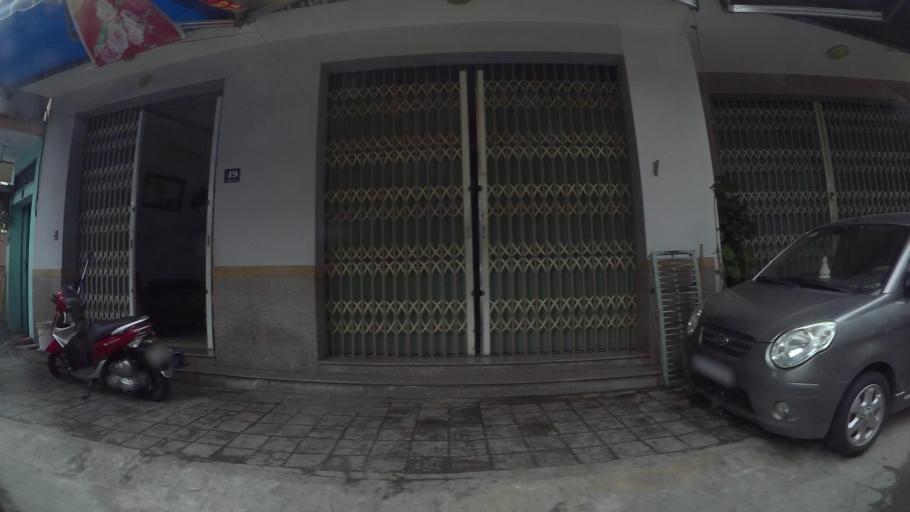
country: VN
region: Da Nang
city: Da Nang
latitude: 16.0763
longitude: 108.2104
